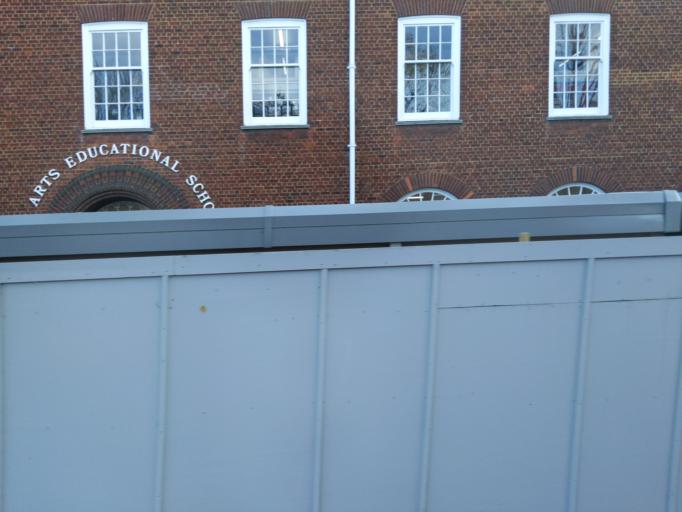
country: GB
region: England
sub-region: Greater London
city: Hammersmith
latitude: 51.4963
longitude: -0.2525
